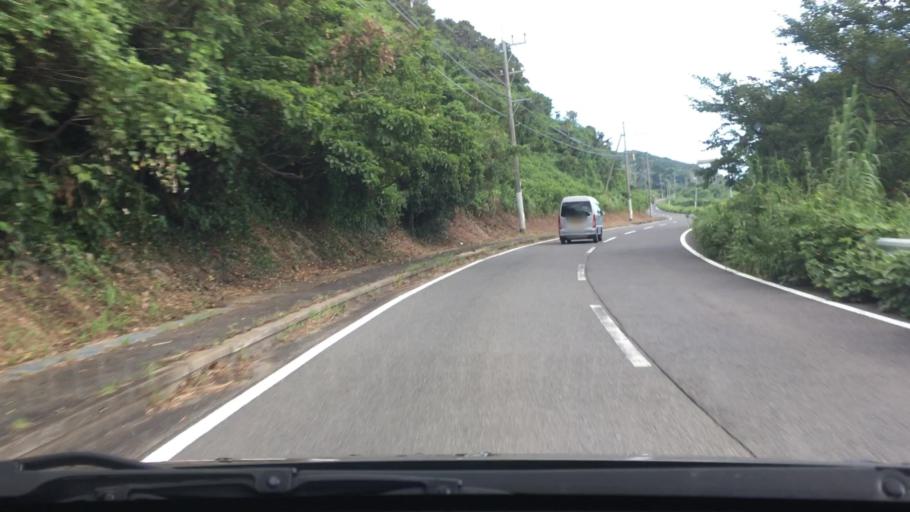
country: JP
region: Nagasaki
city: Togitsu
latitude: 32.8681
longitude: 129.6806
